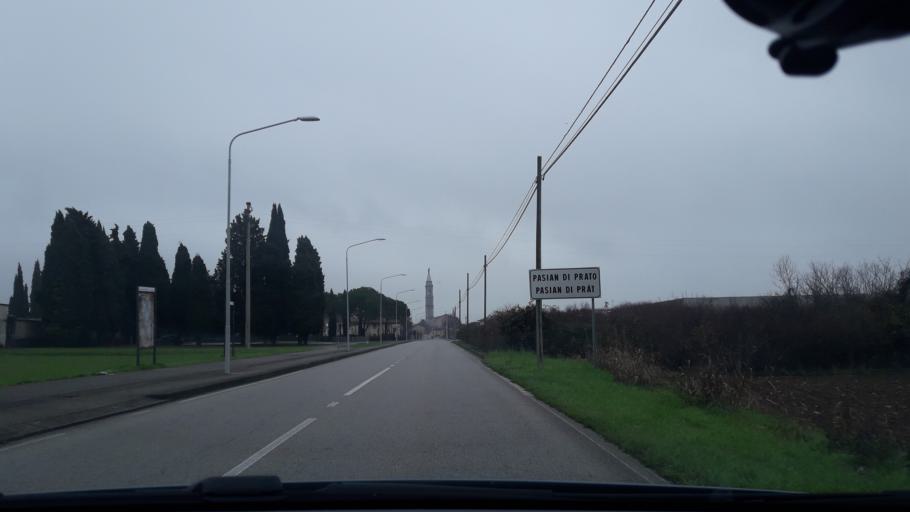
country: IT
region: Friuli Venezia Giulia
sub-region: Provincia di Udine
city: Pasian di Prato
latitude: 46.0505
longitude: 13.1800
